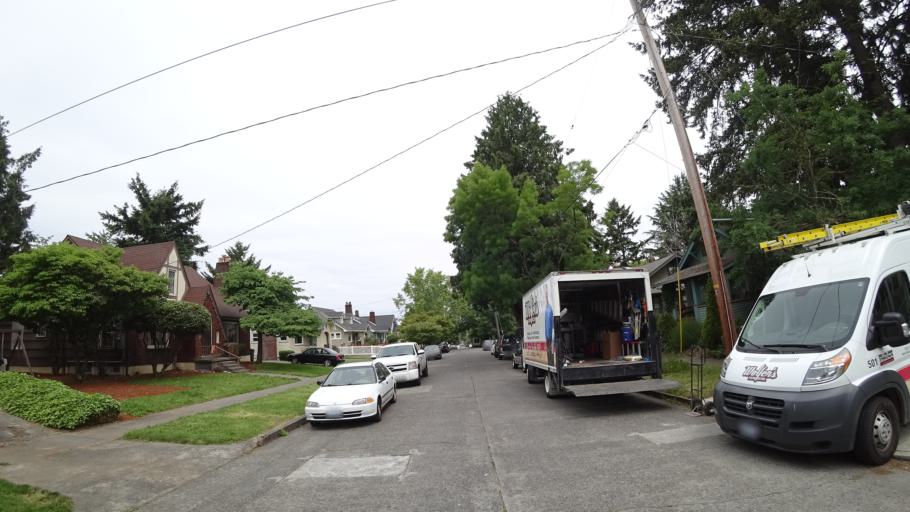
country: US
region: Oregon
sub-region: Multnomah County
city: Portland
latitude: 45.5630
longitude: -122.6403
